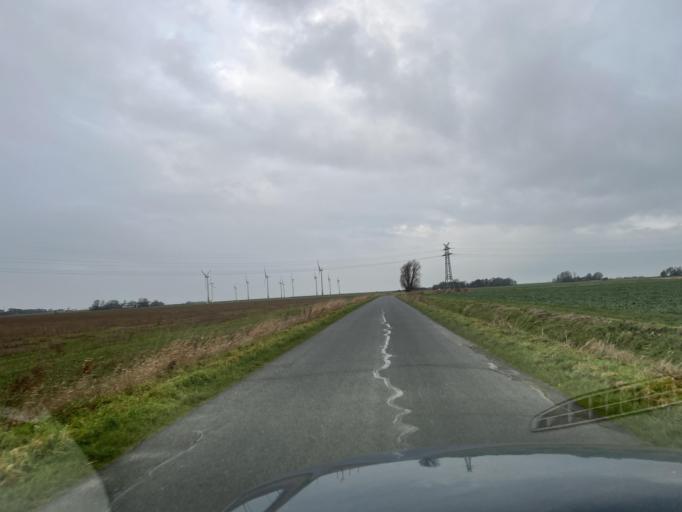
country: DE
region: Schleswig-Holstein
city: Hillgroven
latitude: 54.2143
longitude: 8.8894
